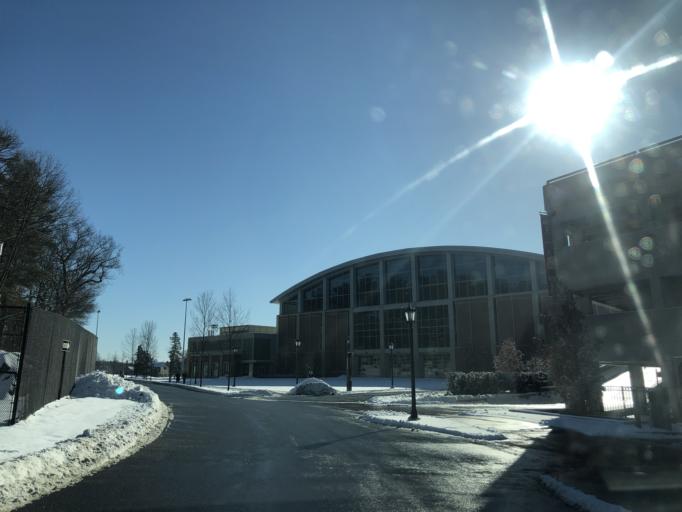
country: US
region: Massachusetts
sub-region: Middlesex County
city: Watertown
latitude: 42.3359
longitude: -71.1655
